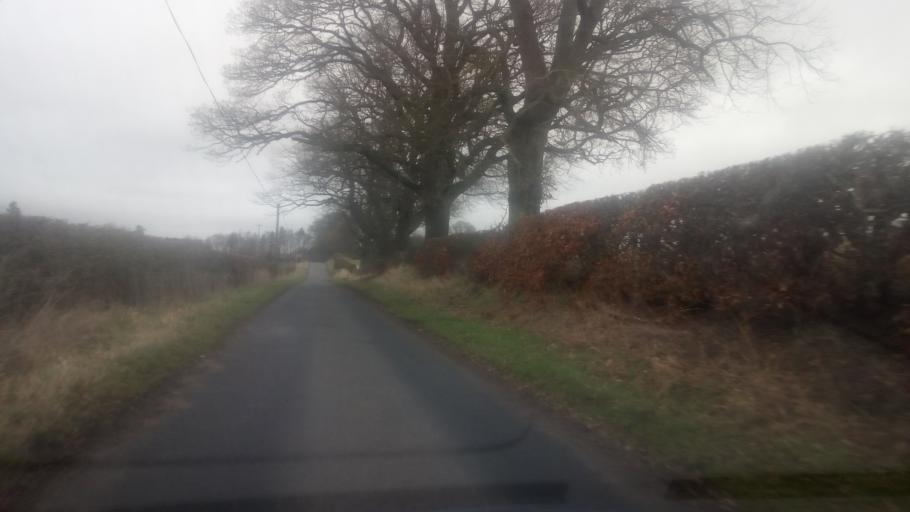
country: GB
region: Scotland
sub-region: The Scottish Borders
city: Jedburgh
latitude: 55.5308
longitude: -2.5059
